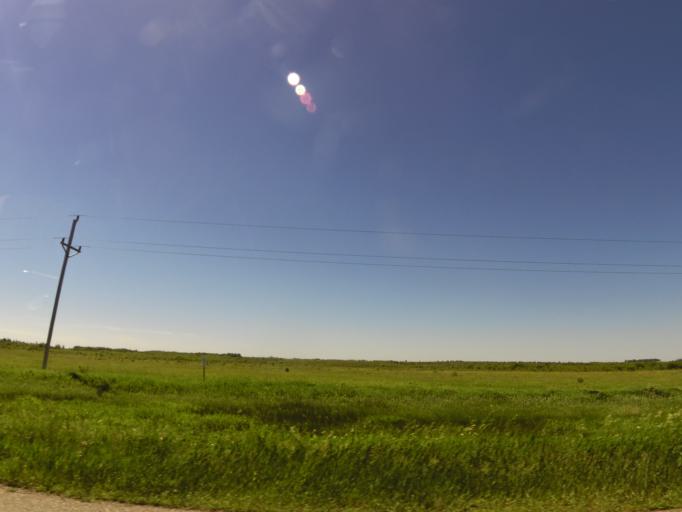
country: US
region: Minnesota
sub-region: Red Lake County
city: Red Lake Falls
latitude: 47.7603
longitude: -96.3568
